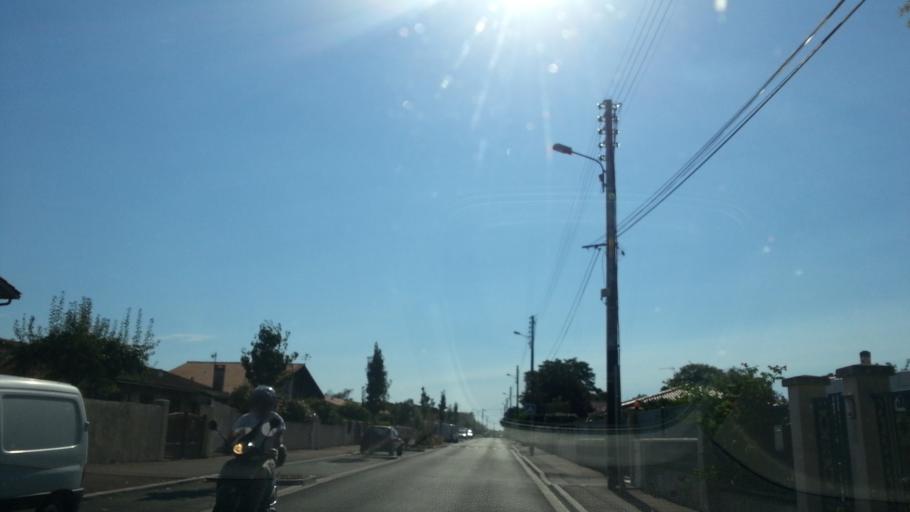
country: FR
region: Aquitaine
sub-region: Departement de la Gironde
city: Villenave-d'Ornon
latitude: 44.7681
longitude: -0.5742
